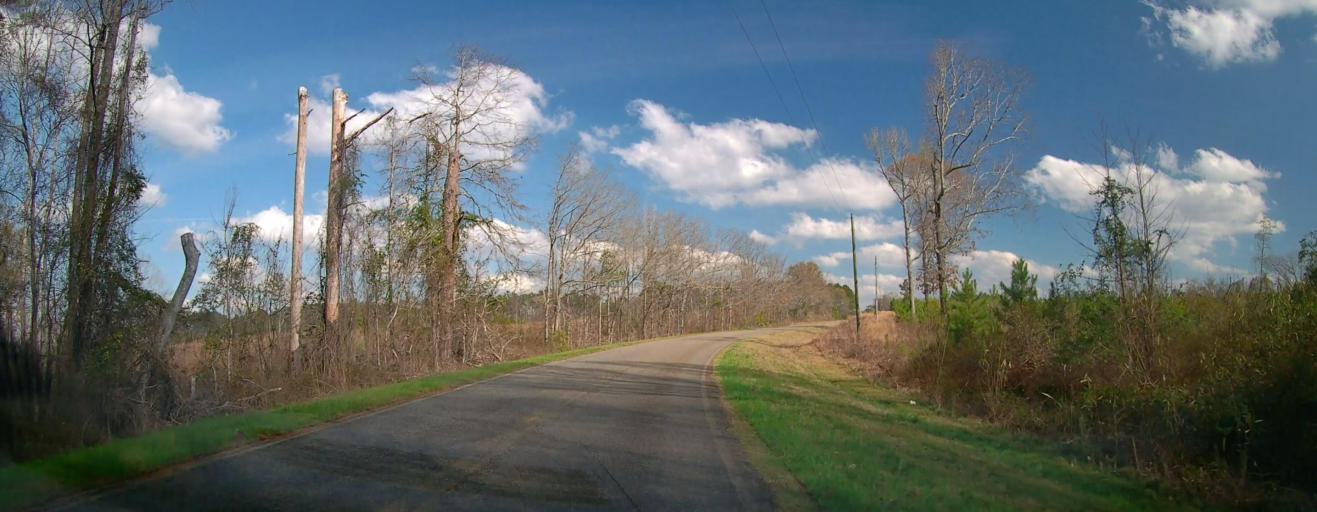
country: US
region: Georgia
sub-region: Wilkinson County
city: Irwinton
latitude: 32.6416
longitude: -83.1721
